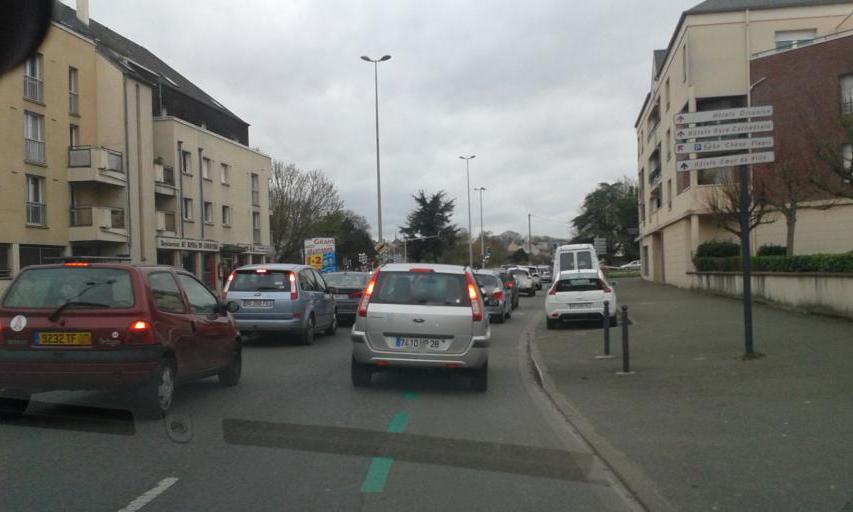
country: FR
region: Centre
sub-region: Departement d'Eure-et-Loir
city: Chartres
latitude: 48.4445
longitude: 1.4976
